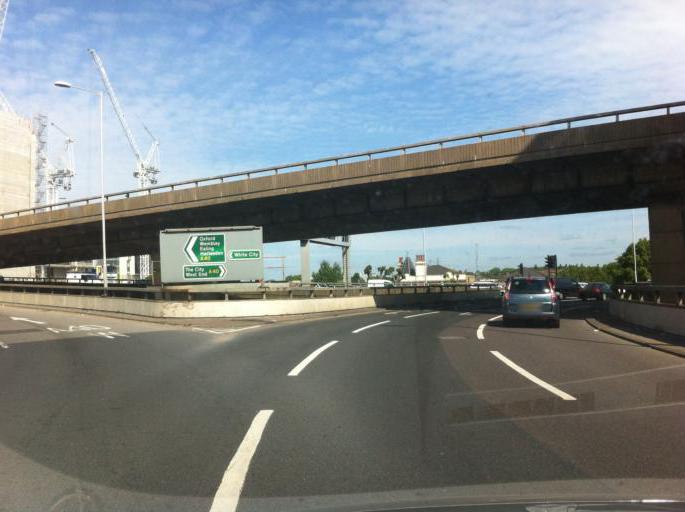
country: GB
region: England
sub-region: Greater London
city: Hammersmith
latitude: 51.5135
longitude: -0.2213
